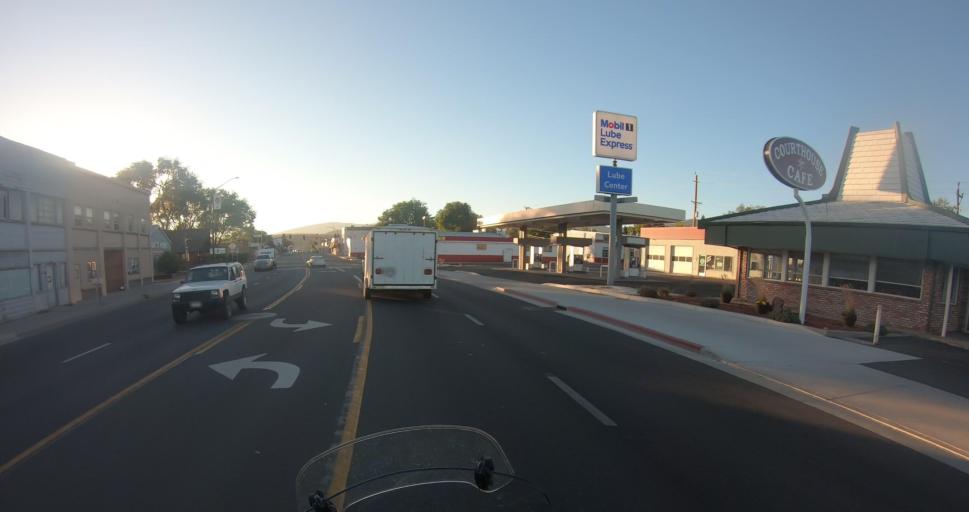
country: US
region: California
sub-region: Lassen County
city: Susanville
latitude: 40.4137
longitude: -120.6403
